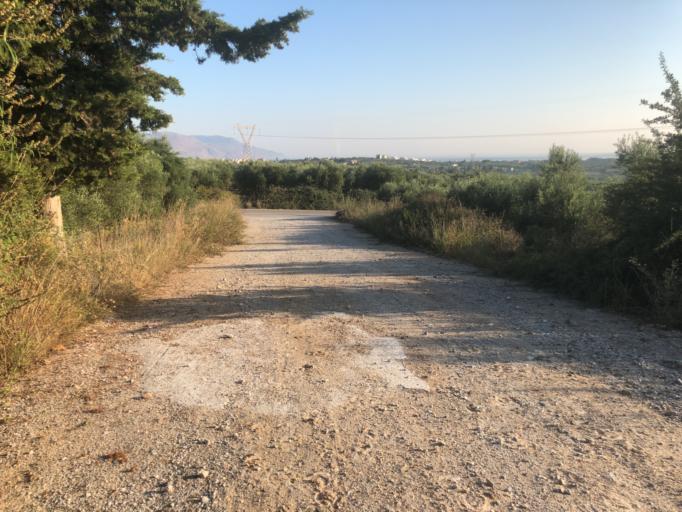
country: GR
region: Crete
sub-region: Nomos Chanias
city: Georgioupolis
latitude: 35.3382
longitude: 24.2896
